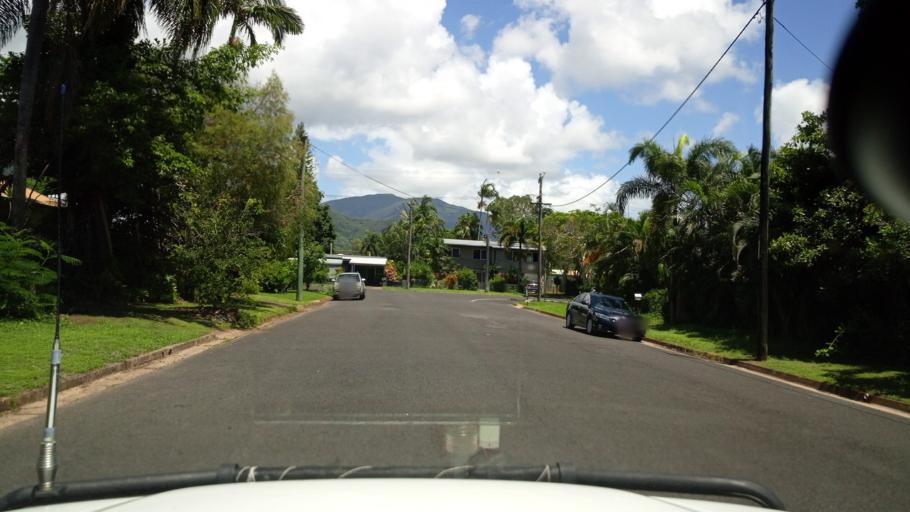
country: AU
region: Queensland
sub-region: Cairns
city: Cairns
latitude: -16.9203
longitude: 145.7491
